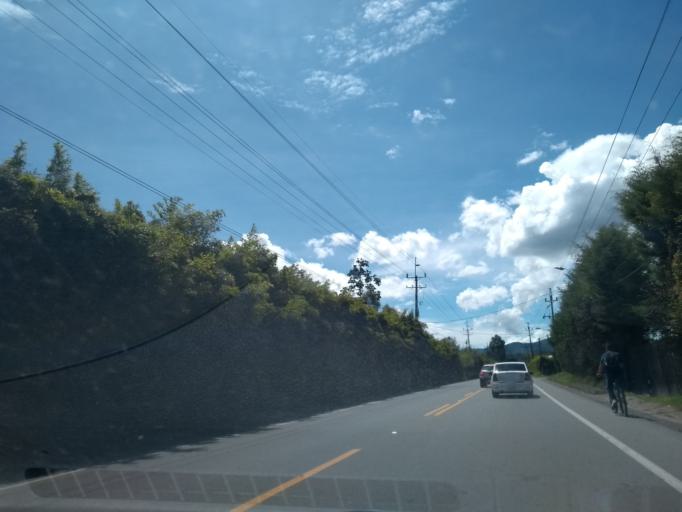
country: CO
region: Antioquia
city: La Ceja
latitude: 6.0441
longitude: -75.3993
